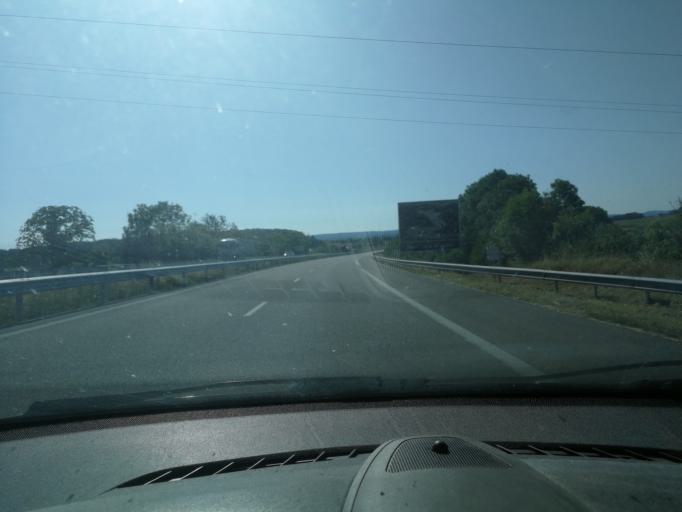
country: FR
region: Alsace
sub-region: Departement du Bas-Rhin
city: Drulingen
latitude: 48.8078
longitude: 7.1721
